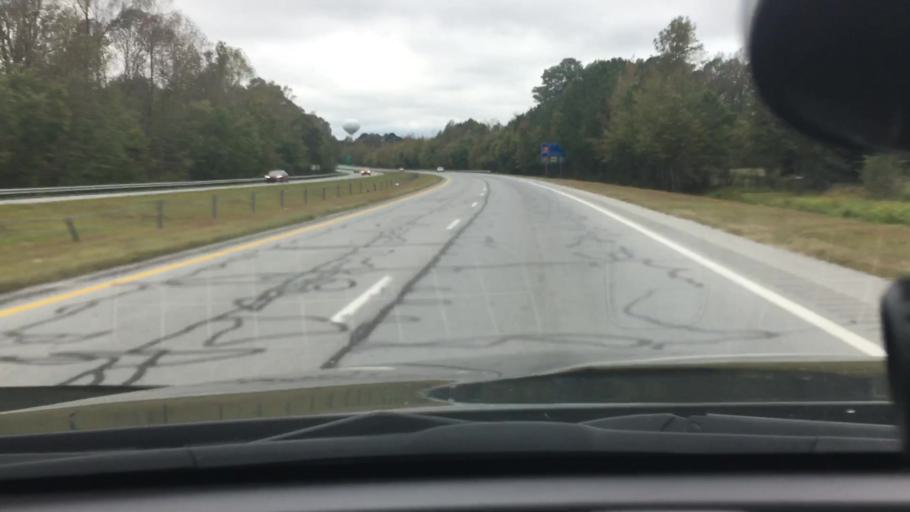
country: US
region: North Carolina
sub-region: Pitt County
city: Farmville
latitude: 35.6203
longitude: -77.5943
